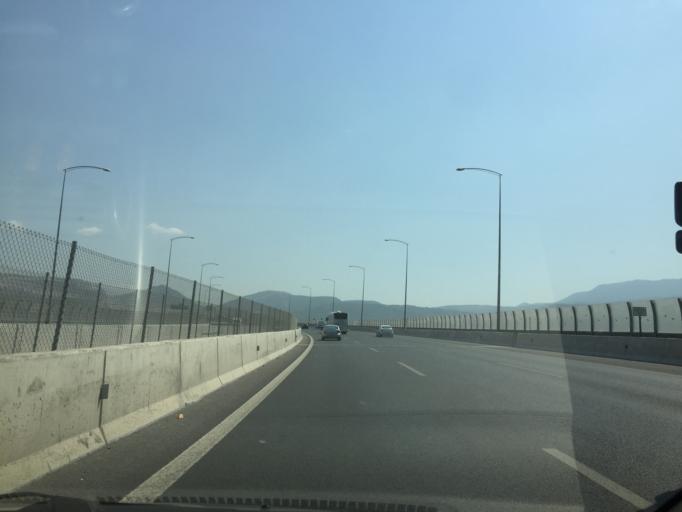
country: TR
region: Izmir
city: Bornova
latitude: 38.4426
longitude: 27.2503
